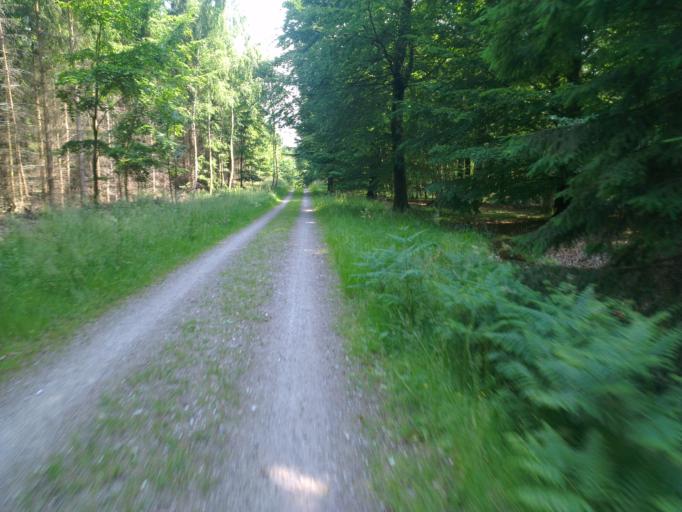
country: DK
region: Capital Region
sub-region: Allerod Kommune
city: Lillerod
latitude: 55.9159
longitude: 12.3657
